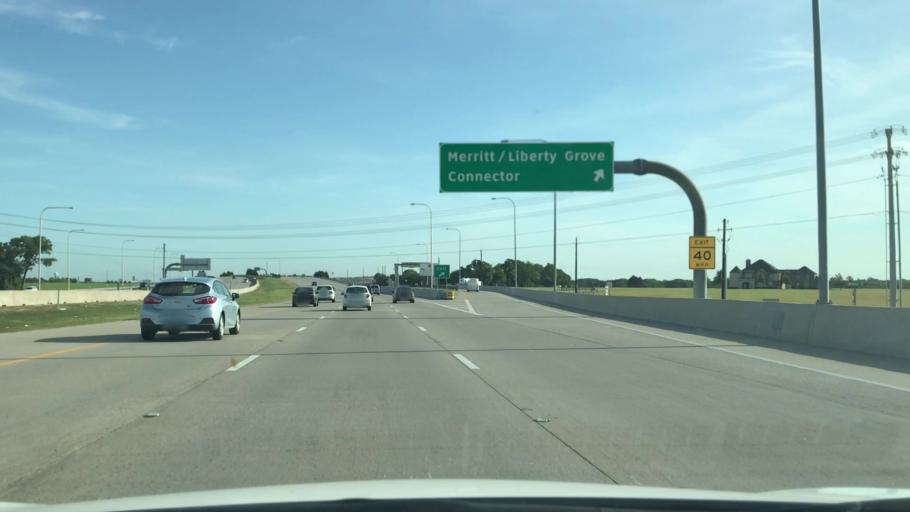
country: US
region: Texas
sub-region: Dallas County
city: Rowlett
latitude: 32.9264
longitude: -96.5526
